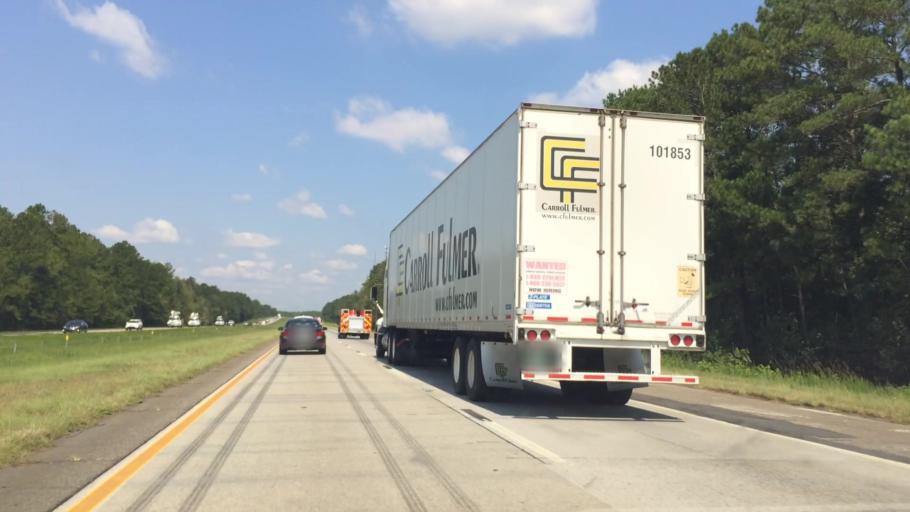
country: US
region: South Carolina
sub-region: Colleton County
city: Walterboro
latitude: 33.0266
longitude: -80.6661
